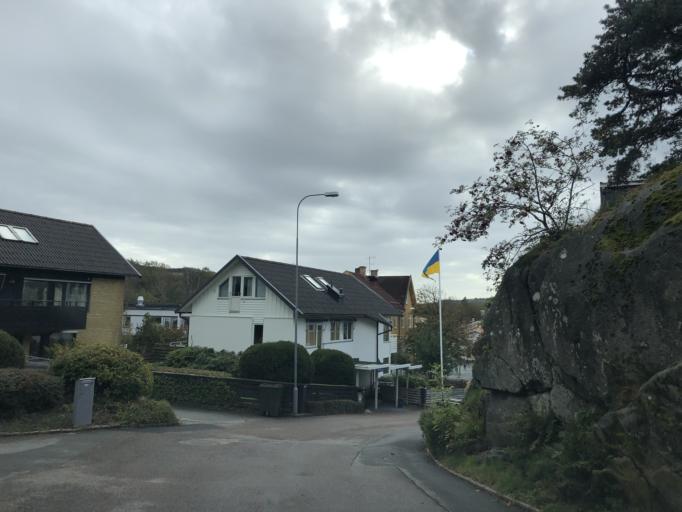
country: SE
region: Vaestra Goetaland
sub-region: Goteborg
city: Majorna
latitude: 57.6706
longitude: 11.8593
